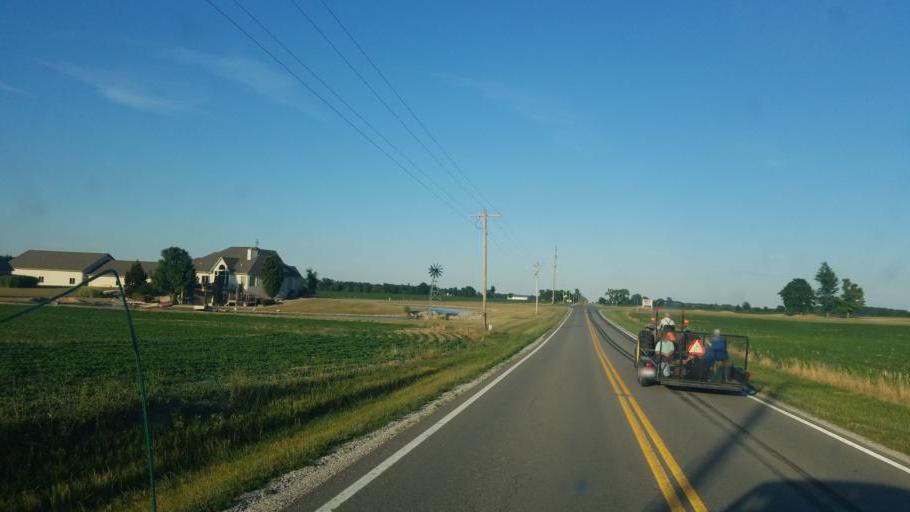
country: US
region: Ohio
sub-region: Williams County
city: Edgerton
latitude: 41.3826
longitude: -84.7695
